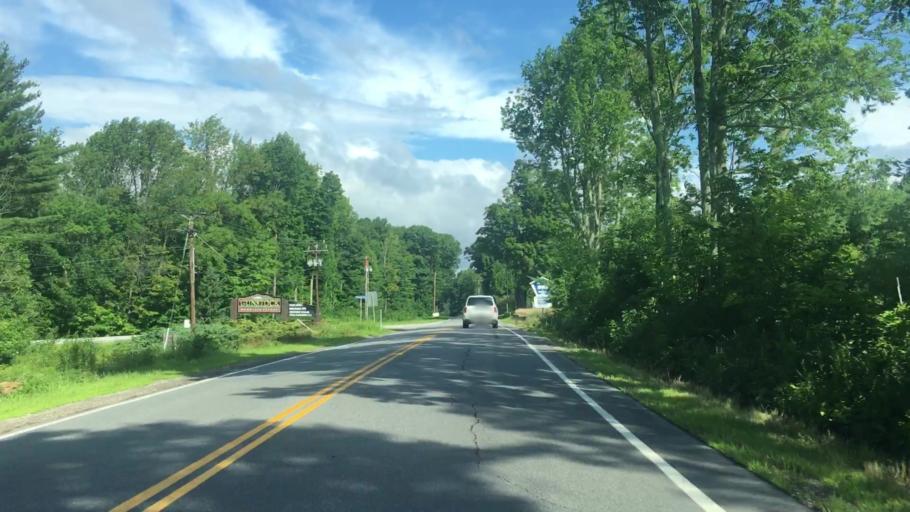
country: US
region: New Hampshire
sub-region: Belknap County
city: Gilford
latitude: 43.5500
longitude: -71.3582
